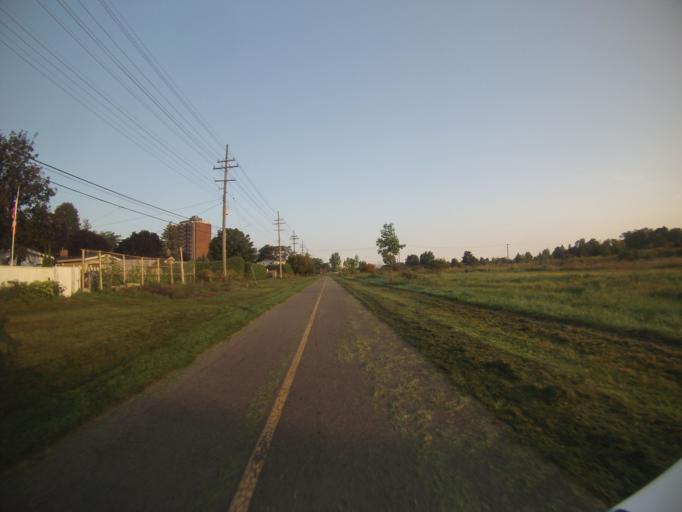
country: CA
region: Ontario
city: Ottawa
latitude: 45.3872
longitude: -75.6366
